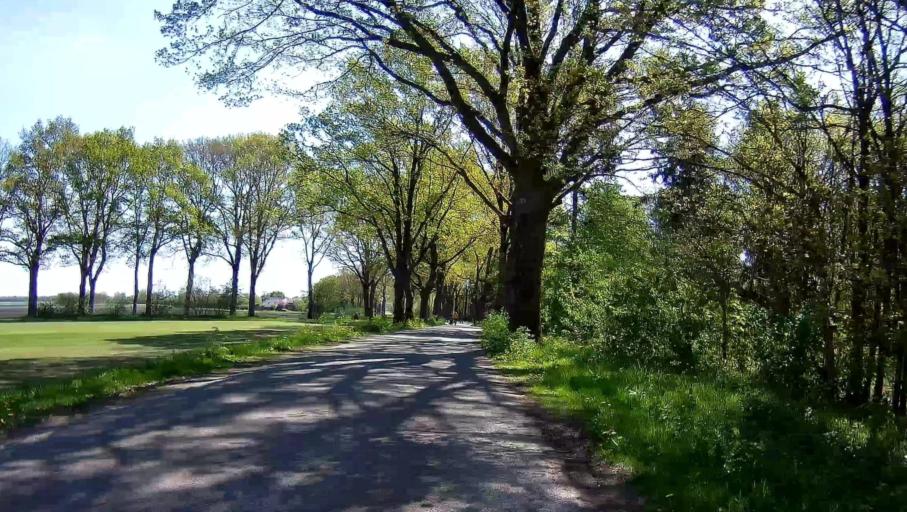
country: NL
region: Drenthe
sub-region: Gemeente Borger-Odoorn
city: Borger
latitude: 52.9708
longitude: 6.8095
